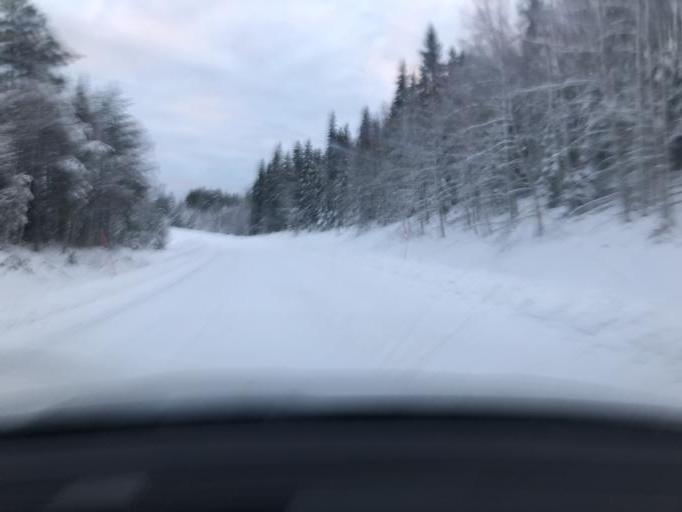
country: SE
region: Vaesternorrland
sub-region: Kramfors Kommun
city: Nordingra
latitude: 62.9954
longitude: 18.2406
